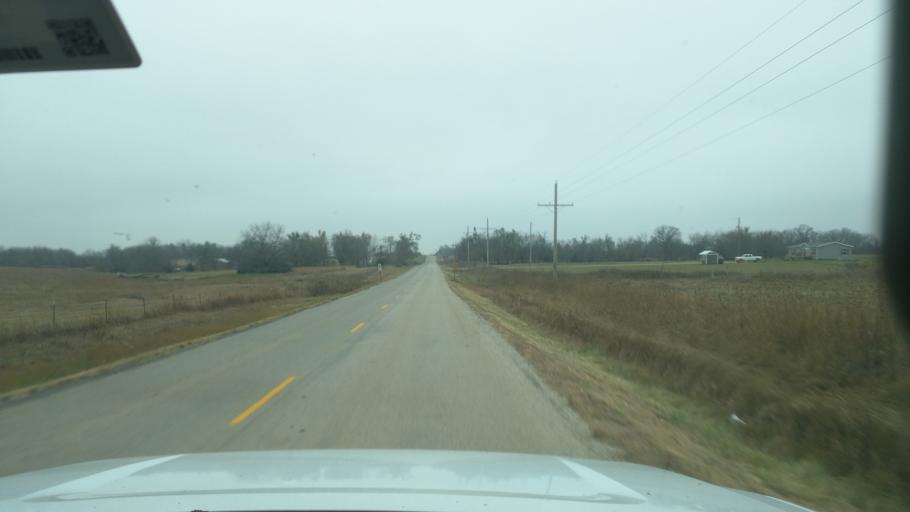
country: US
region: Kansas
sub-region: Morris County
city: Council Grove
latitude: 38.6292
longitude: -96.2614
